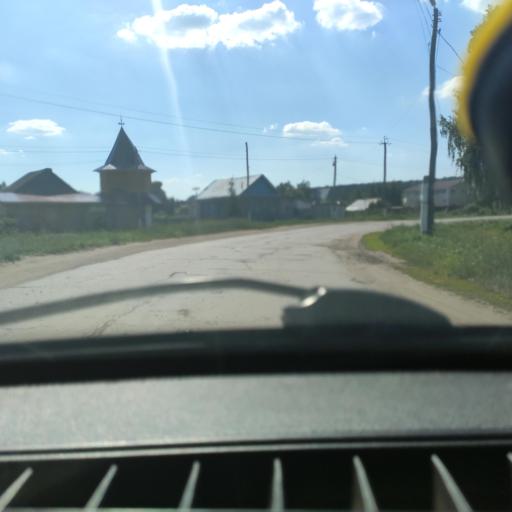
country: RU
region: Samara
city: Povolzhskiy
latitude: 53.7528
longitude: 49.7374
